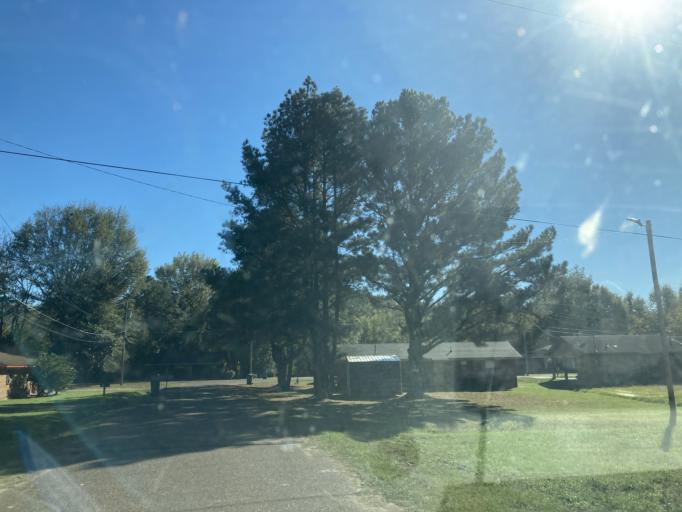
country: US
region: Mississippi
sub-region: Yazoo County
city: Yazoo City
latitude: 32.8431
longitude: -90.4232
